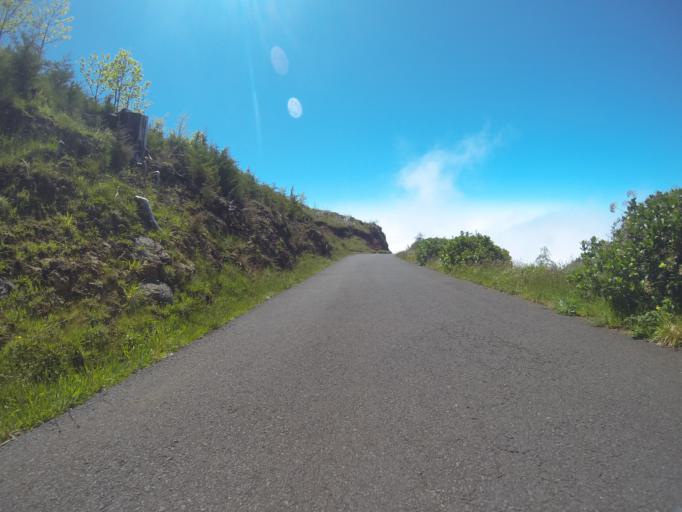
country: PT
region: Madeira
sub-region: Funchal
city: Nossa Senhora do Monte
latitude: 32.7016
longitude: -16.9135
